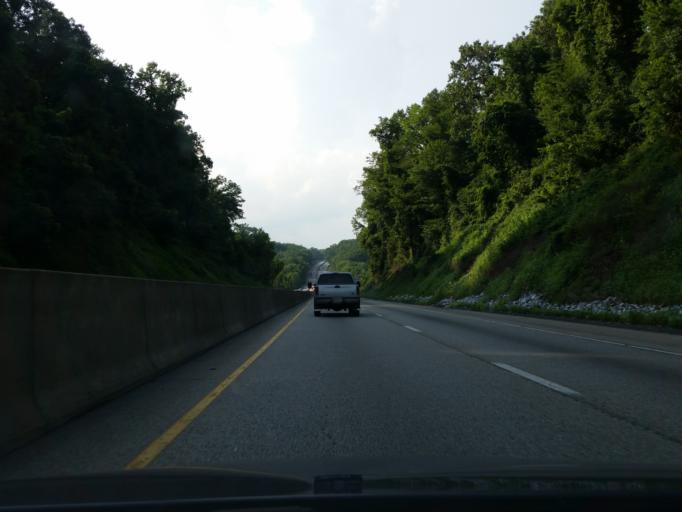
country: US
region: Pennsylvania
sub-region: York County
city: Valley Green
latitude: 40.0994
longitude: -76.7764
